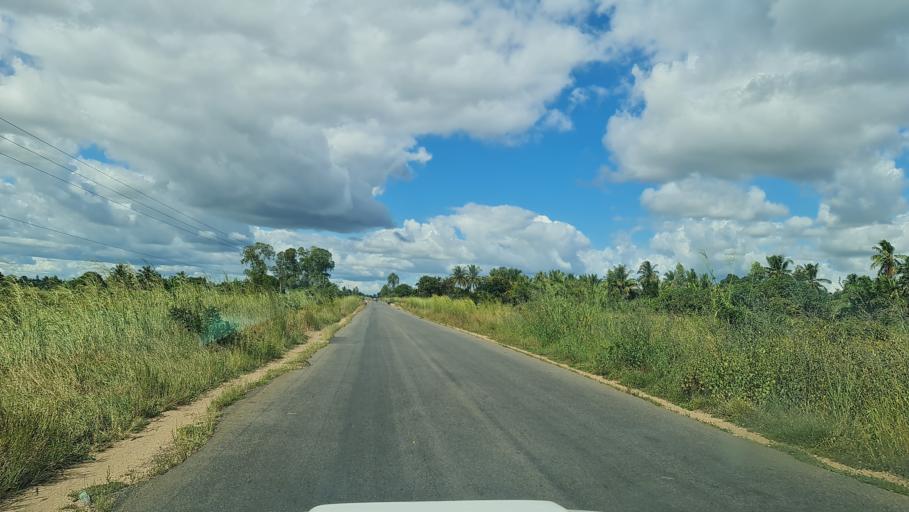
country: MZ
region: Zambezia
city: Quelimane
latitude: -17.5883
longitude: 36.7566
